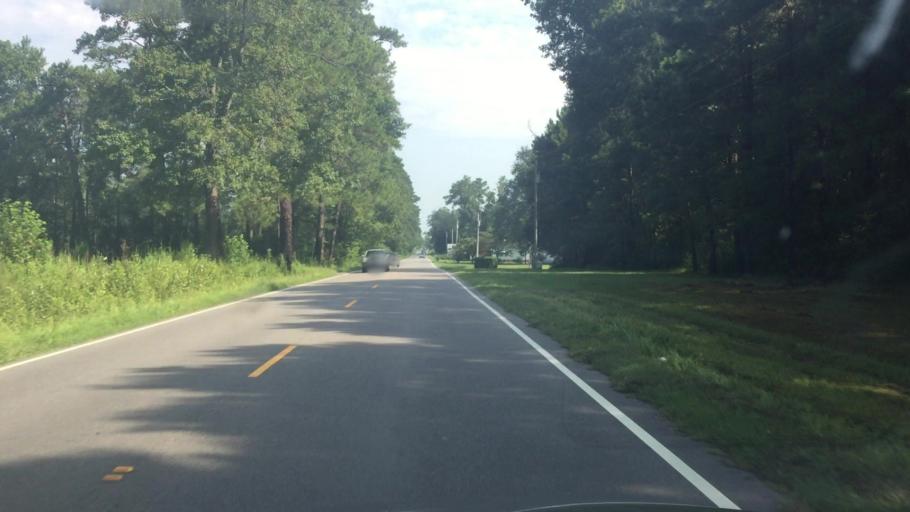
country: US
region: North Carolina
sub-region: Columbus County
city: Chadbourn
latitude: 34.2969
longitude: -78.8264
